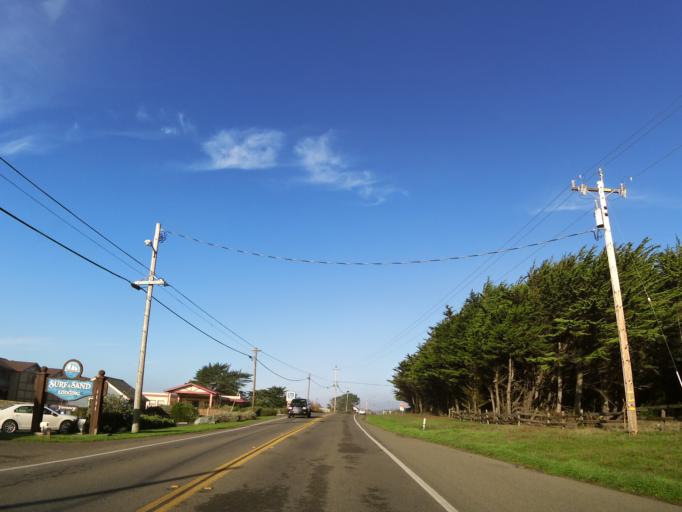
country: US
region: California
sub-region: Mendocino County
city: Fort Bragg
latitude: 39.4623
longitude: -123.8059
